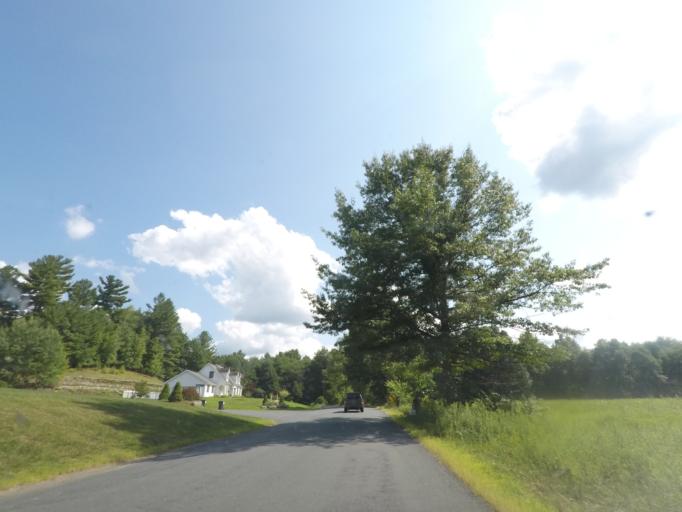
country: US
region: New York
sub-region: Rensselaer County
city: West Sand Lake
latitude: 42.6409
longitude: -73.5930
